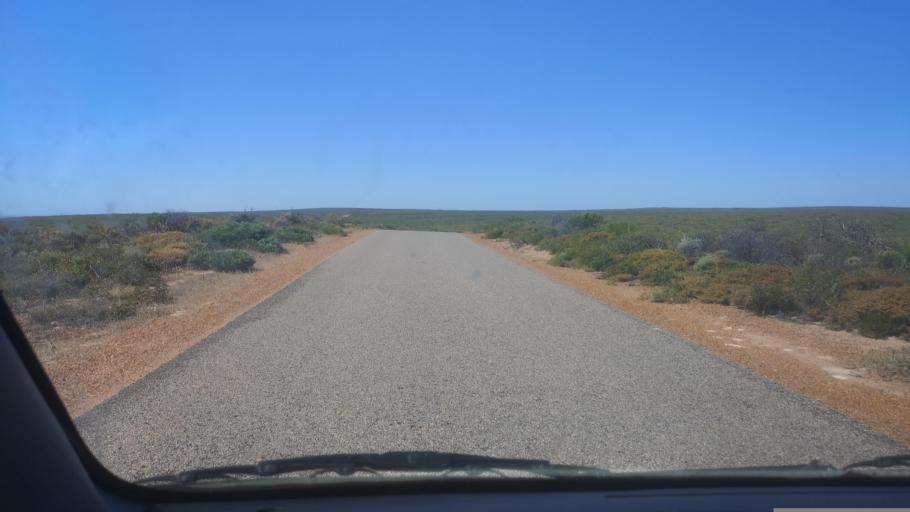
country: AU
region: Western Australia
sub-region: Northampton Shire
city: Kalbarri
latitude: -27.8171
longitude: 114.1175
